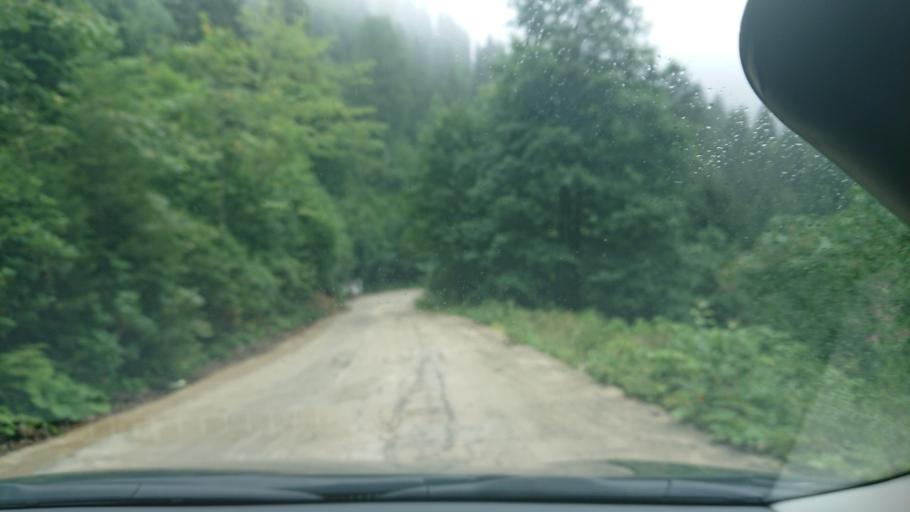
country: TR
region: Gumushane
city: Kurtun
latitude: 40.6603
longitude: 39.0260
